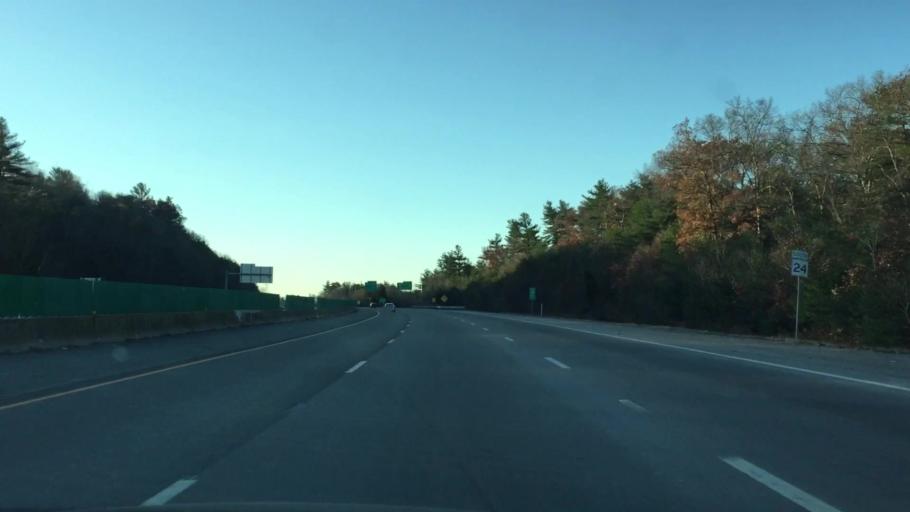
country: US
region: Massachusetts
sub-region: Bristol County
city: Raynham Center
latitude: 41.9634
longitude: -71.0283
